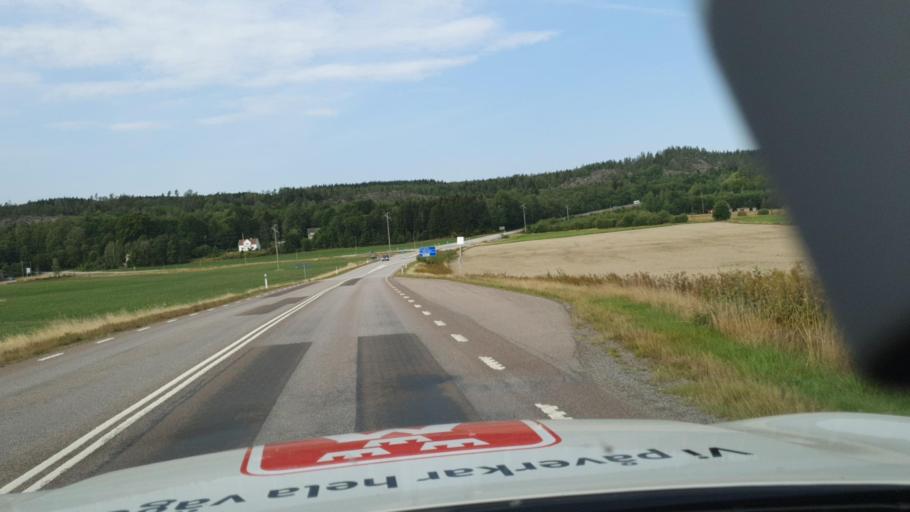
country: SE
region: Vaestra Goetaland
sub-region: Melleruds Kommun
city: Mellerud
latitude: 58.7278
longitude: 12.3708
